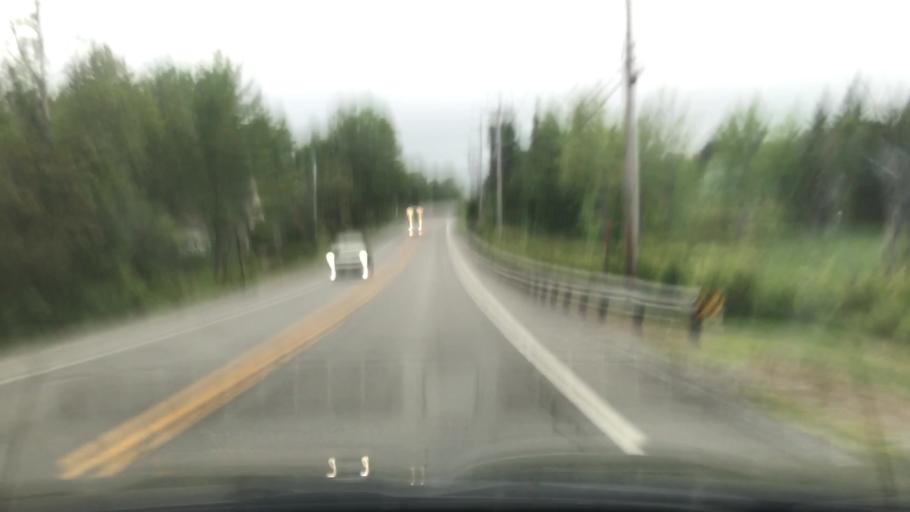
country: US
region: Maine
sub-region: Hancock County
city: Trenton
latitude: 44.4048
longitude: -68.3438
